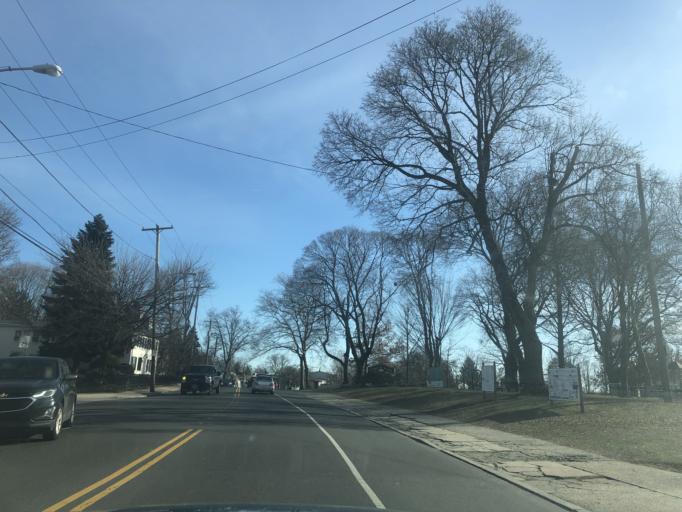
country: US
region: Pennsylvania
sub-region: Montgomery County
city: Bala-Cynwyd
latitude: 40.0374
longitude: -75.2210
